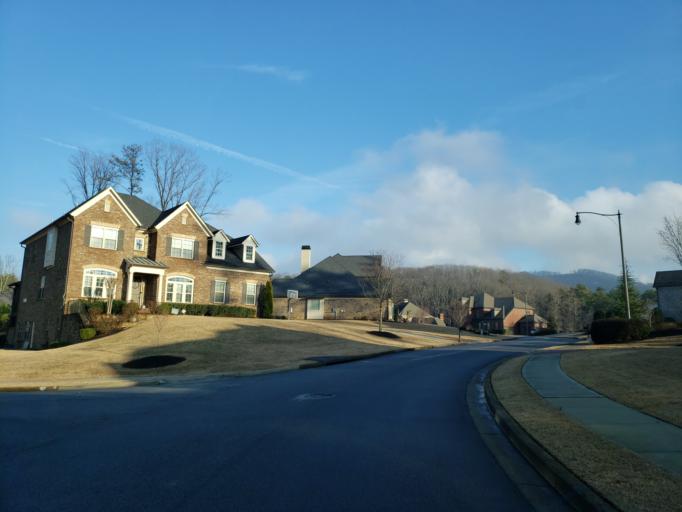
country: US
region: Georgia
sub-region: Cobb County
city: Kennesaw
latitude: 33.9879
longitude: -84.5926
